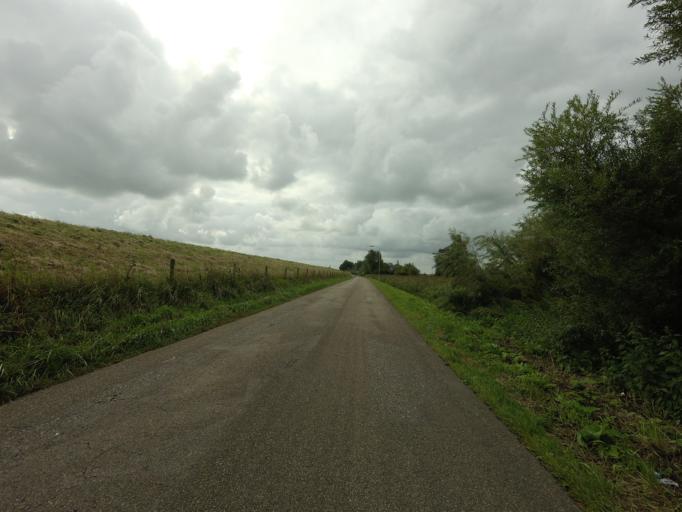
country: NL
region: North Holland
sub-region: Gemeente Hoorn
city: Hoorn
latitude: 52.5998
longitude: 5.0186
